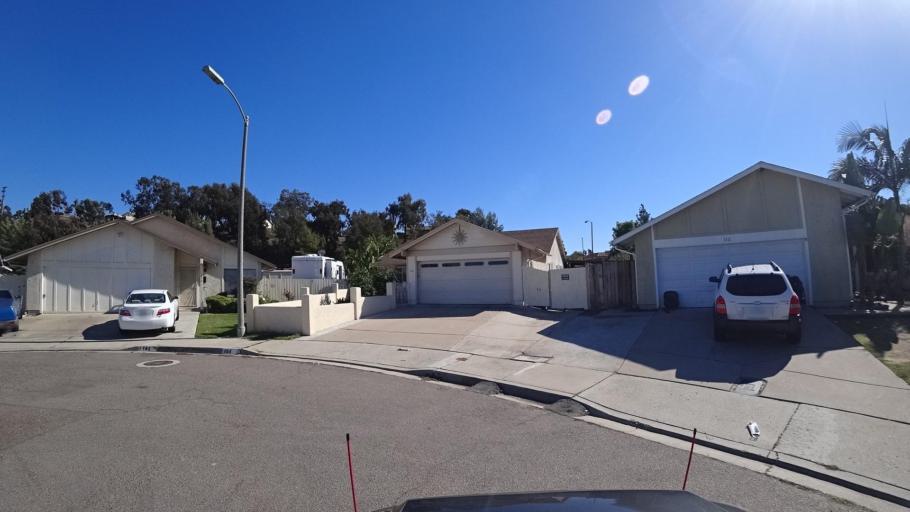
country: US
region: California
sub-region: San Diego County
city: La Presa
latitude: 32.6984
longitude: -117.0179
